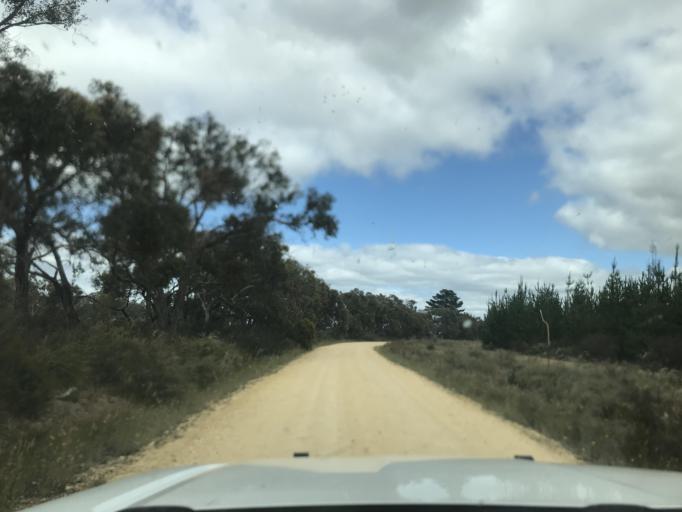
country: AU
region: South Australia
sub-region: Wattle Range
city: Penola
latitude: -37.3186
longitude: 141.1407
